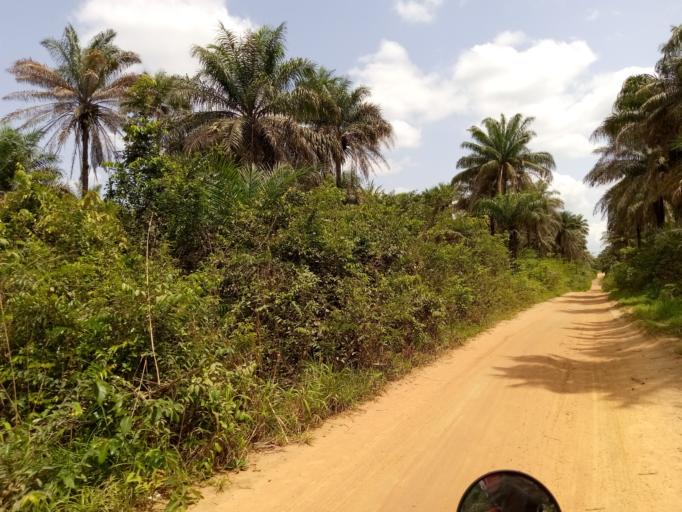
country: SL
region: Western Area
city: Waterloo
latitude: 8.4256
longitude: -13.0096
